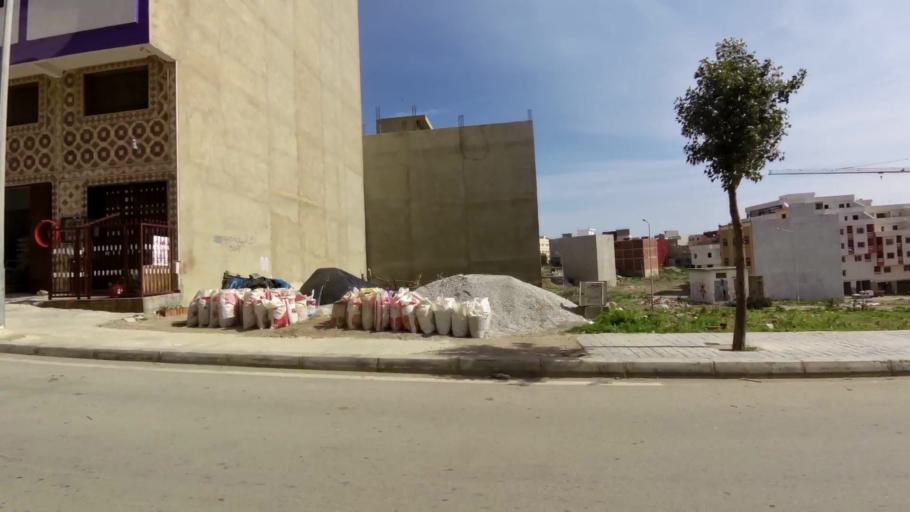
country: MA
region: Tanger-Tetouan
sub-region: Tanger-Assilah
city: Tangier
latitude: 35.7281
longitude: -5.8106
